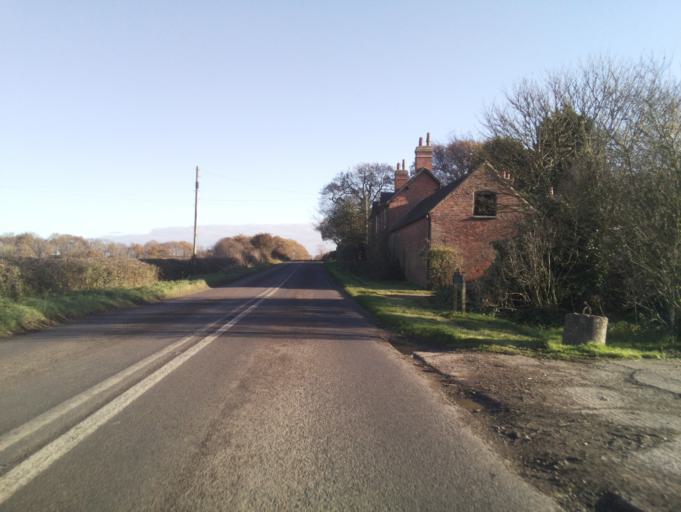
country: GB
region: England
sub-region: Staffordshire
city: Barton under Needwood
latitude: 52.8186
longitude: -1.7717
